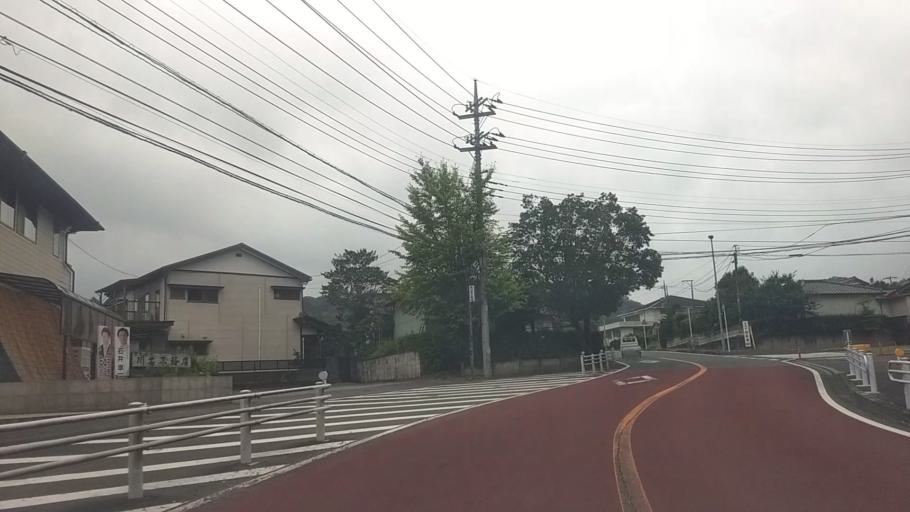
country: JP
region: Chiba
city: Kisarazu
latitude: 35.2891
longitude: 140.0837
